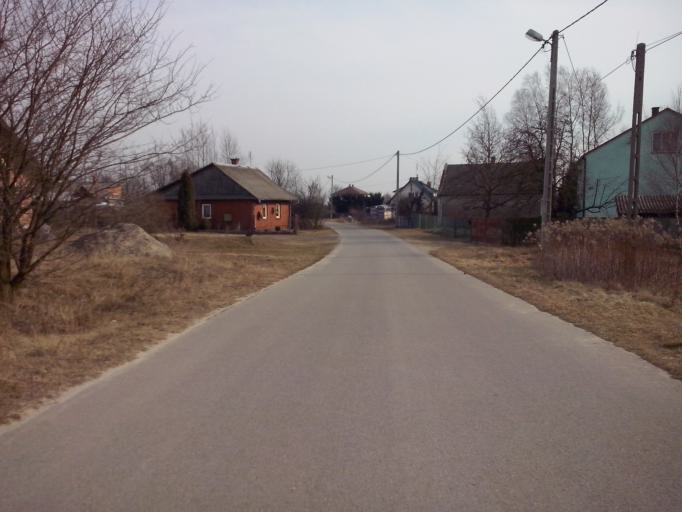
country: PL
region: Subcarpathian Voivodeship
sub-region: Powiat nizanski
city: Krzeszow
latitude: 50.4235
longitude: 22.3627
